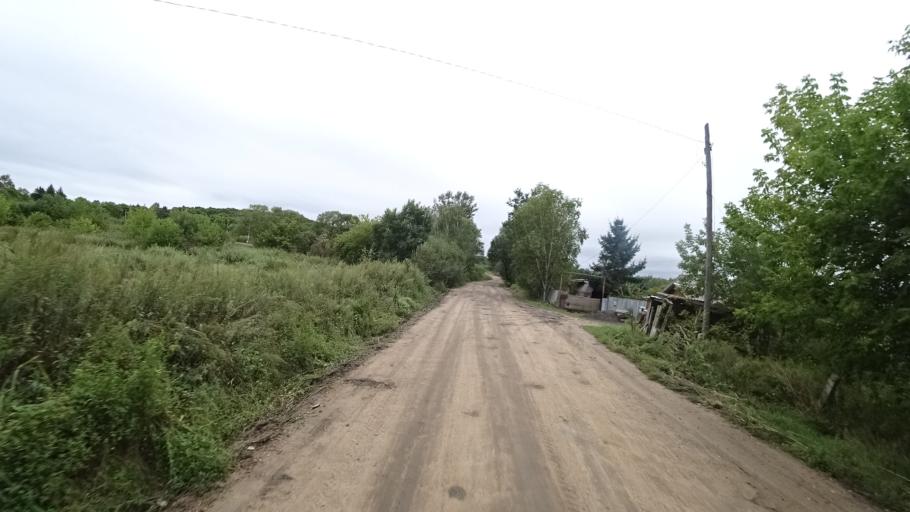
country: RU
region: Primorskiy
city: Rettikhovka
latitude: 44.1644
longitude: 132.7417
